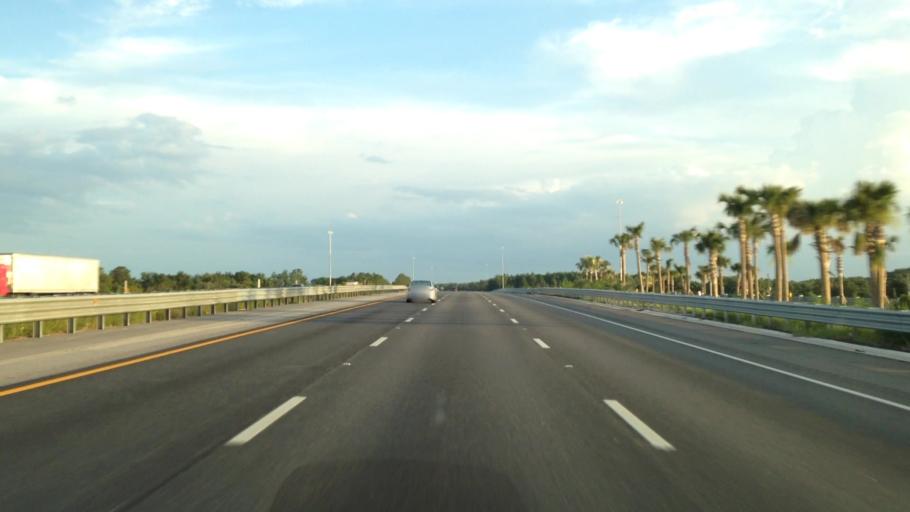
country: US
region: Florida
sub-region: Pasco County
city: San Antonio
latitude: 28.3275
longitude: -82.3246
